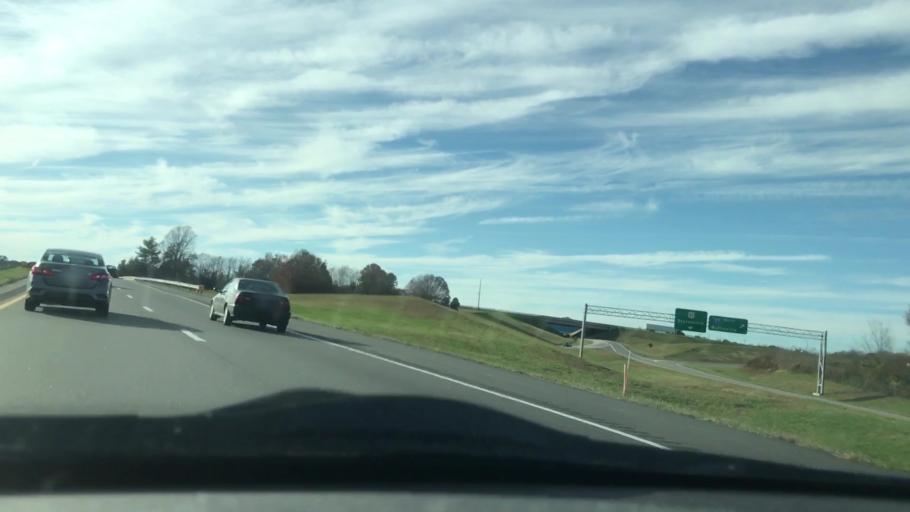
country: US
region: North Carolina
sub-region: Iredell County
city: Statesville
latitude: 35.8091
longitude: -80.8568
